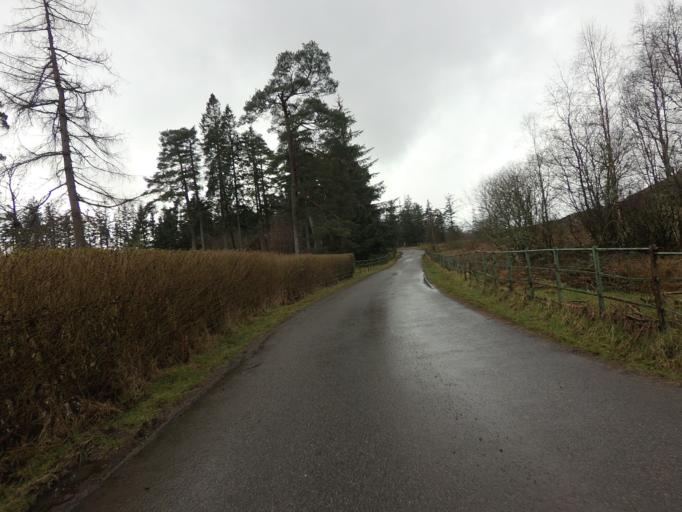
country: GB
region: Scotland
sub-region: West Dunbartonshire
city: Balloch
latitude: 56.2587
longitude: -4.5810
